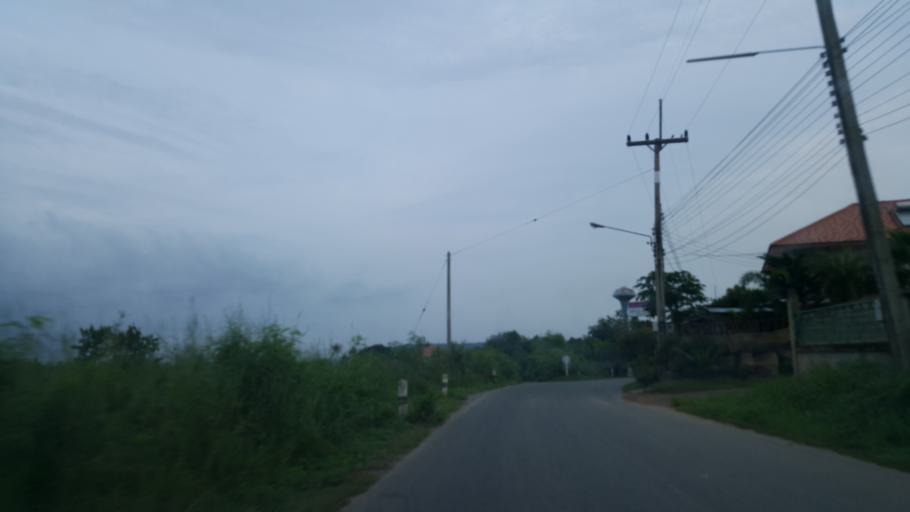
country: TH
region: Chon Buri
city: Sattahip
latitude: 12.7069
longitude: 100.9077
